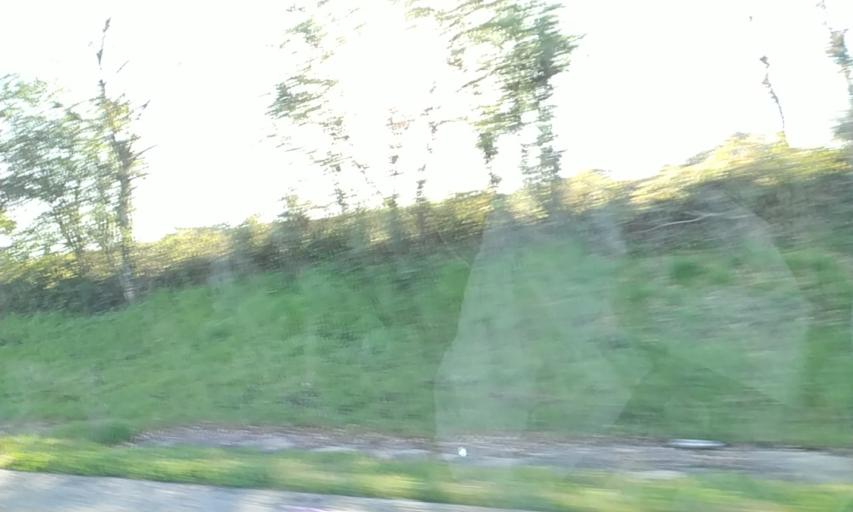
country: ES
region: Galicia
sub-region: Provincia de Lugo
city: Lugo
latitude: 42.9811
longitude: -7.5016
